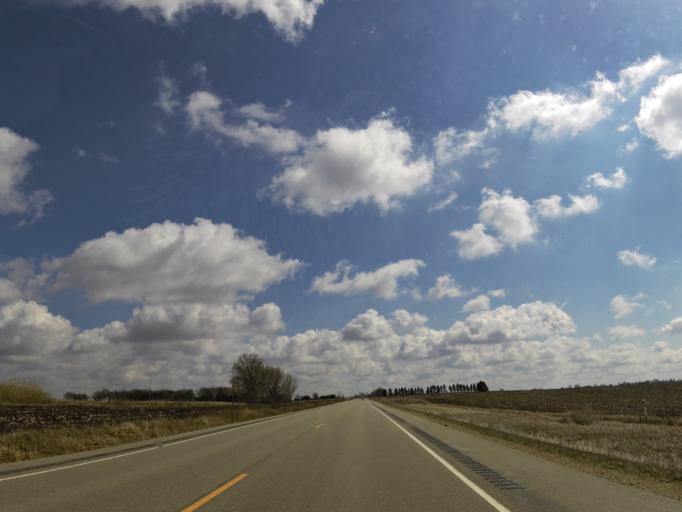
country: US
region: Minnesota
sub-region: Goodhue County
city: Kenyon
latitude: 44.1729
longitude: -92.9048
